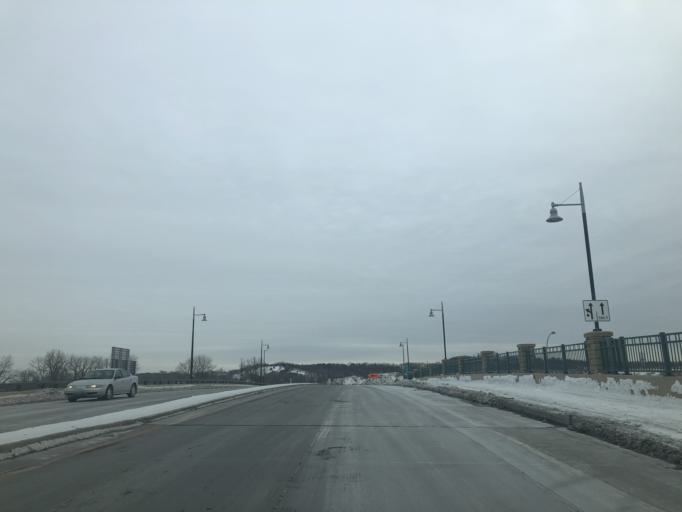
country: US
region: Minnesota
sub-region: Ramsey County
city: Mounds View
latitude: 45.0954
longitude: -93.1890
